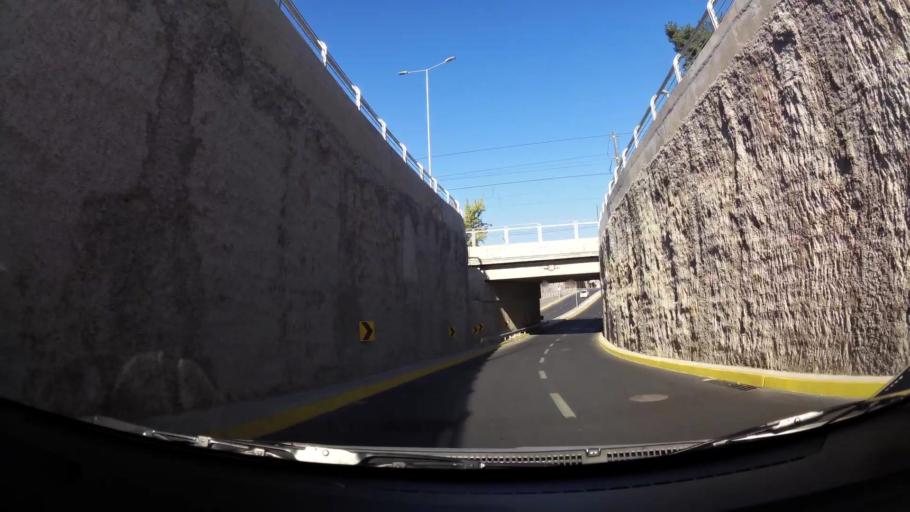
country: CL
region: Maule
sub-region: Provincia de Curico
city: Curico
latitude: -34.9878
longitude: -71.2456
